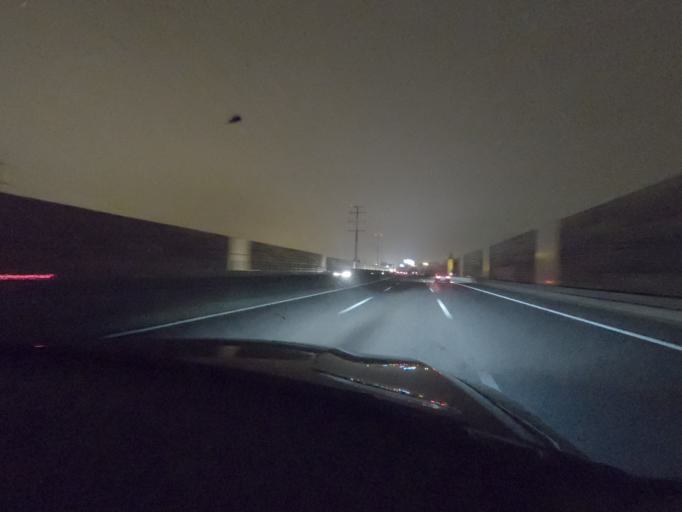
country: PT
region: Lisbon
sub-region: Loures
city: Santa Iria da Azoia
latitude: 38.8401
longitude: -9.0947
